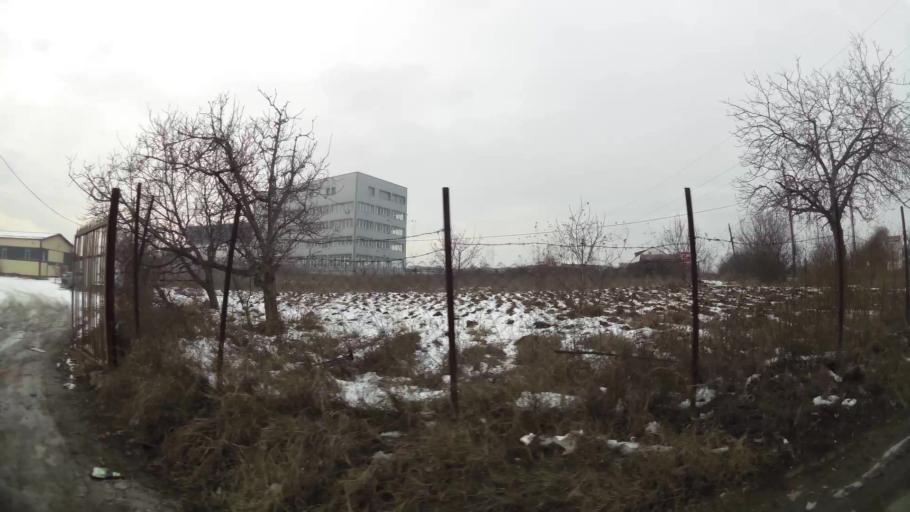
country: MK
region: Suto Orizari
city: Suto Orizare
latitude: 42.0481
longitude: 21.4284
